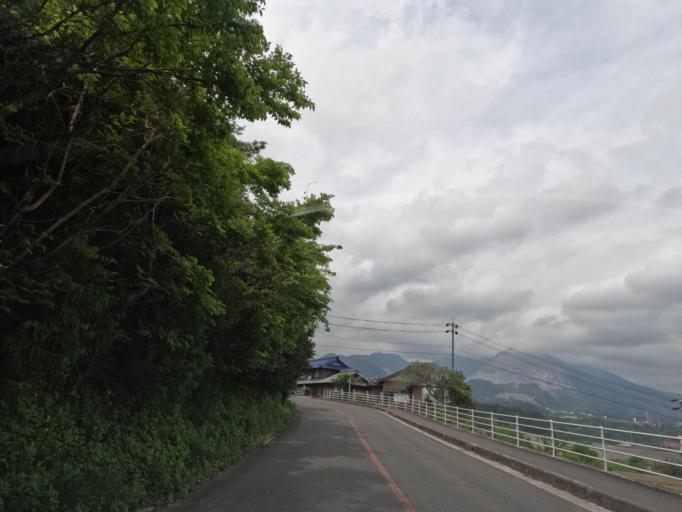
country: JP
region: Mie
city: Komono
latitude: 35.1418
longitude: 136.5178
